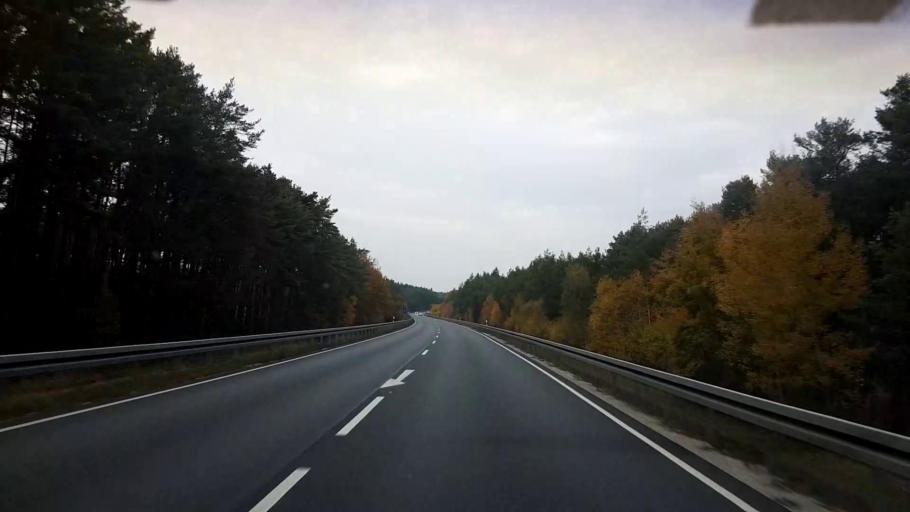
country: DE
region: Bavaria
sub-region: Regierungsbezirk Mittelfranken
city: Hochstadt an der Aisch
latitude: 49.7350
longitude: 10.8268
